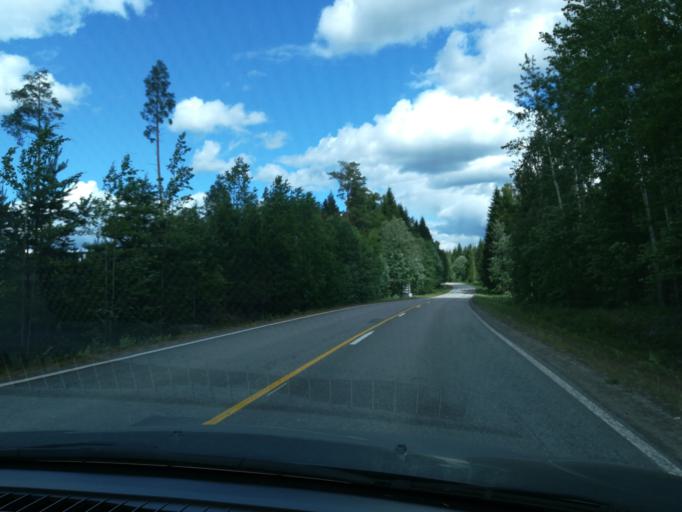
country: FI
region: Southern Savonia
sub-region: Mikkeli
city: Hirvensalmi
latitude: 61.6207
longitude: 26.7828
